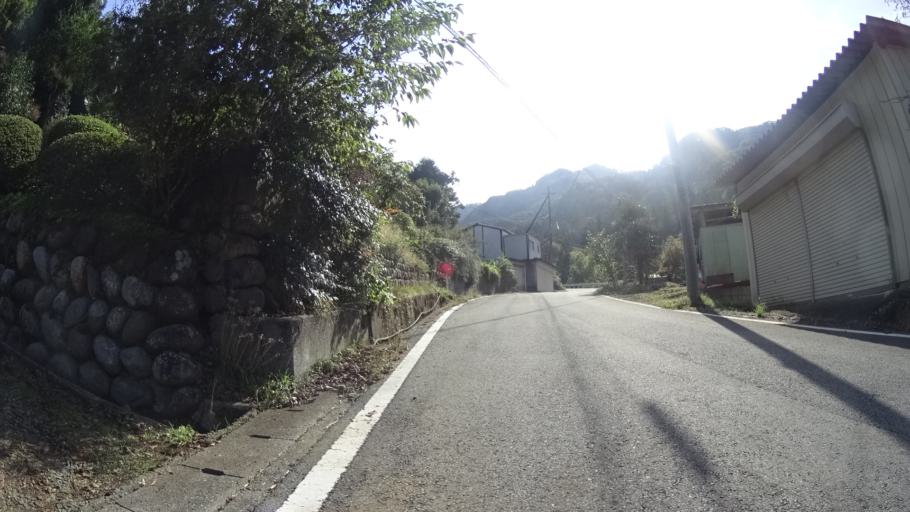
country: JP
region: Yamanashi
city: Otsuki
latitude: 35.5838
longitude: 138.9697
